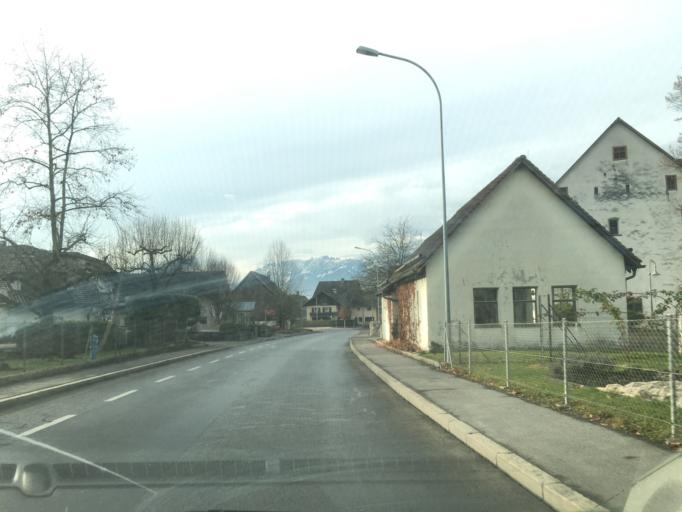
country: AT
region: Vorarlberg
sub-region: Politischer Bezirk Feldkirch
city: Viktorsberg
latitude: 47.2910
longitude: 9.6640
